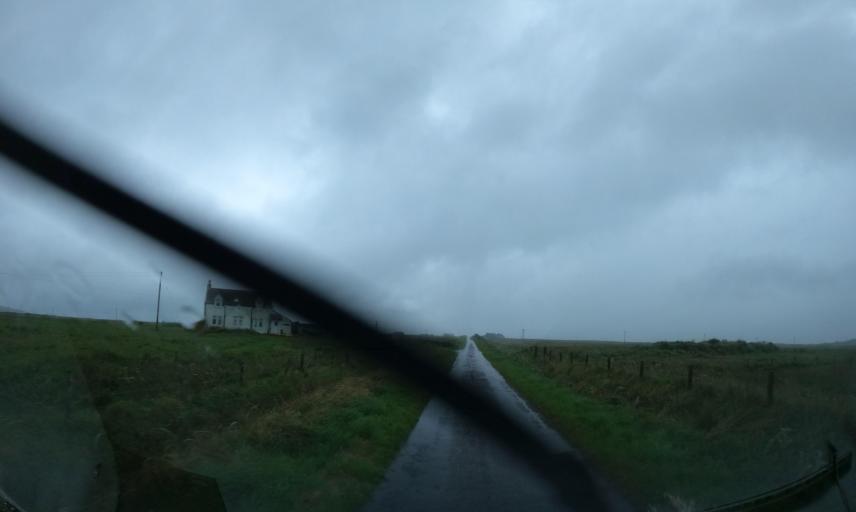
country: GB
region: Scotland
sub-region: Eilean Siar
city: Barra
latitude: 56.4738
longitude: -6.9151
